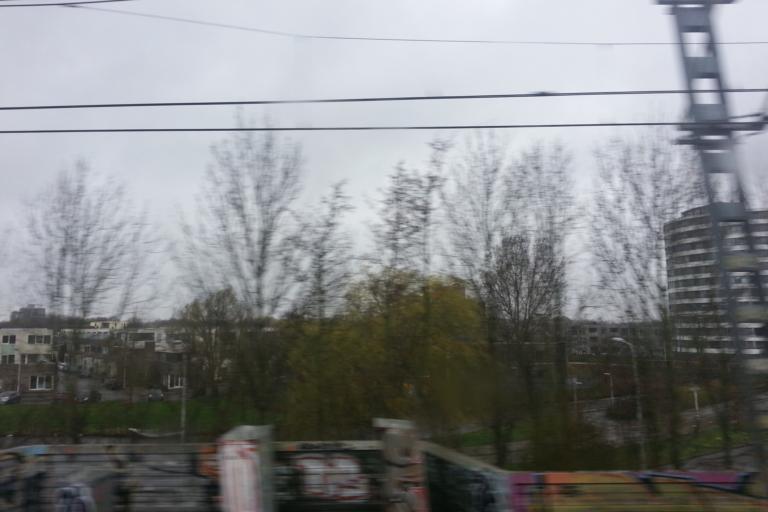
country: NL
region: South Holland
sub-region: Gemeente Voorschoten
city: Voorschoten
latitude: 52.1490
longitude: 4.4585
